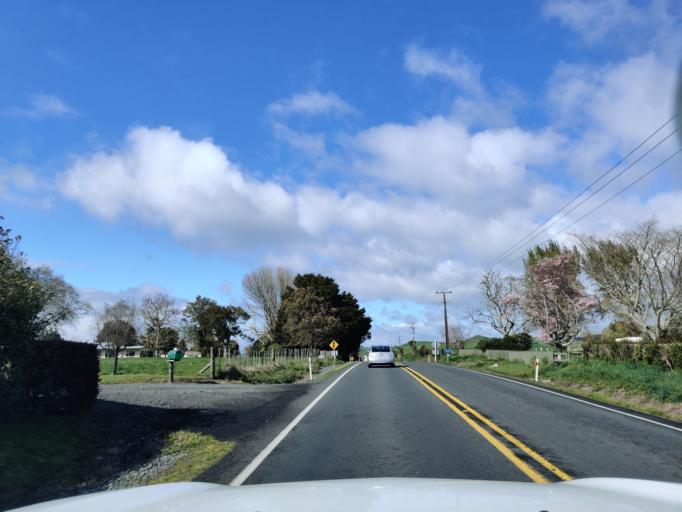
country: NZ
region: Waikato
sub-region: Otorohanga District
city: Otorohanga
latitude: -38.1004
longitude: 175.1893
